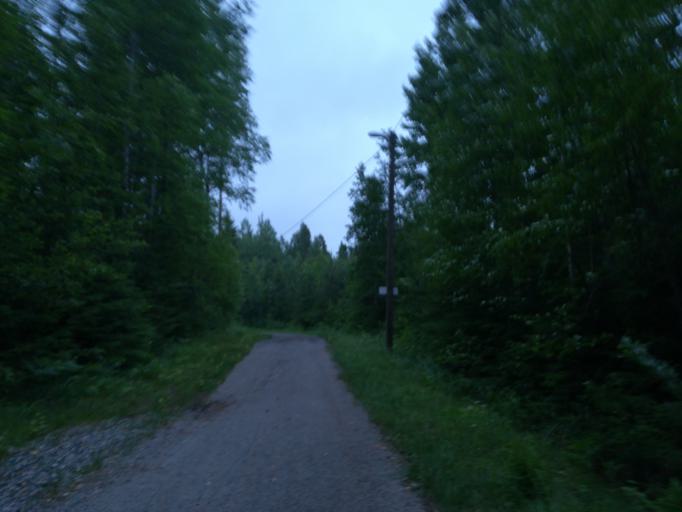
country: FI
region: Southern Savonia
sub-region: Mikkeli
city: Ristiina
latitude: 61.4851
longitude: 27.2818
